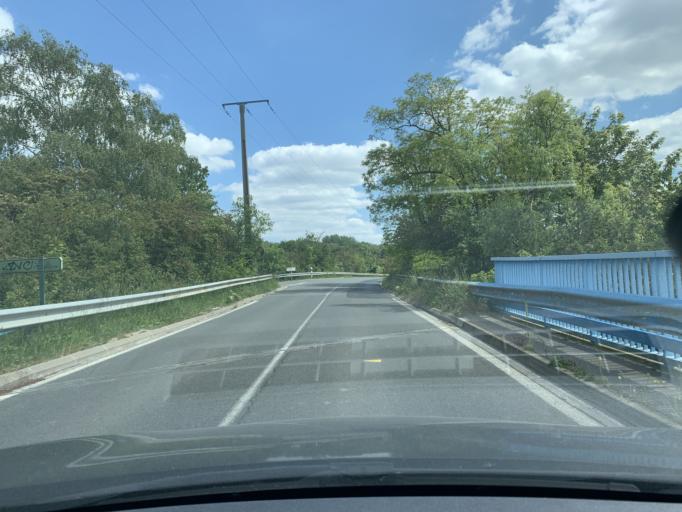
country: FR
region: Nord-Pas-de-Calais
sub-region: Departement du Nord
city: Arleux
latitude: 50.2632
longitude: 3.1025
